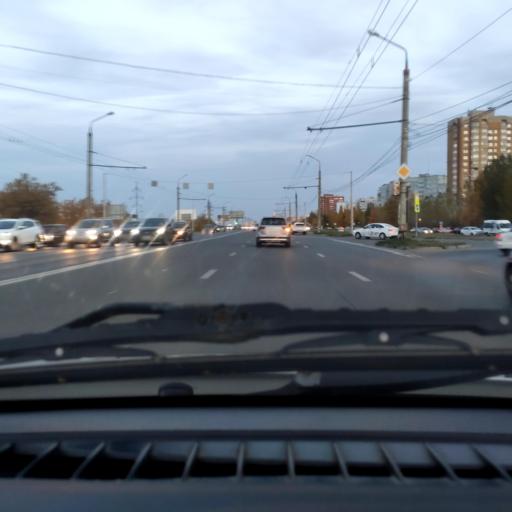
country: RU
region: Samara
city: Tol'yatti
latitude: 53.5494
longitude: 49.3322
